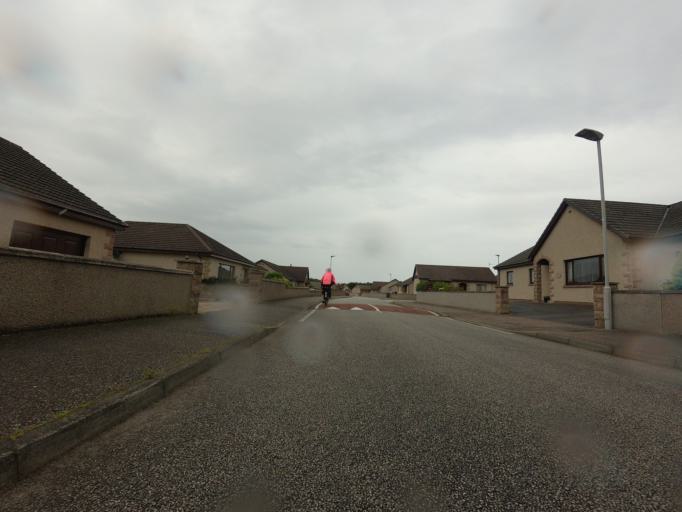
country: GB
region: Scotland
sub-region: Moray
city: Cullen
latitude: 57.6846
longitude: -2.8152
